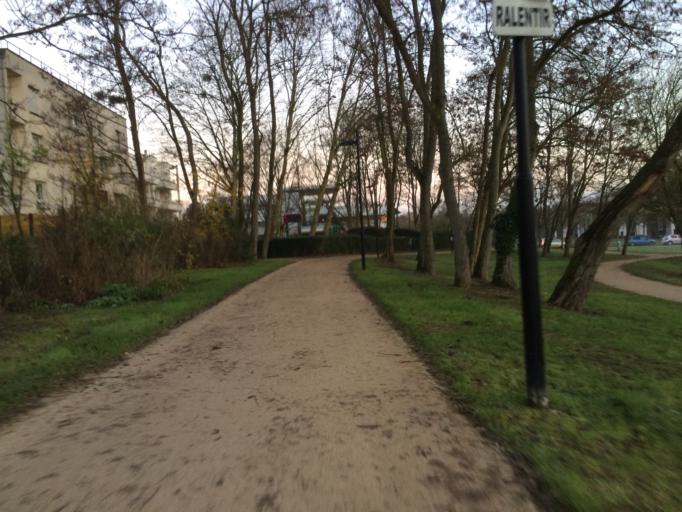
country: FR
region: Ile-de-France
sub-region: Departement des Hauts-de-Seine
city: Sceaux
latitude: 48.7681
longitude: 2.2847
